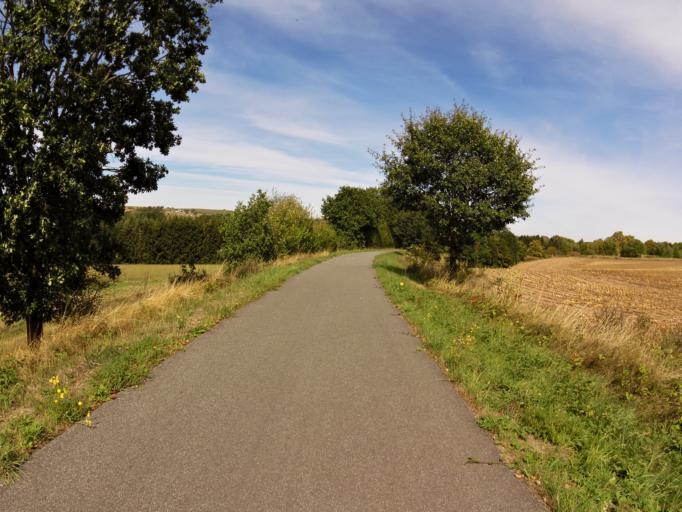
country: DE
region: Rheinland-Pfalz
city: Kesfeld
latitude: 50.1253
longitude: 6.2616
